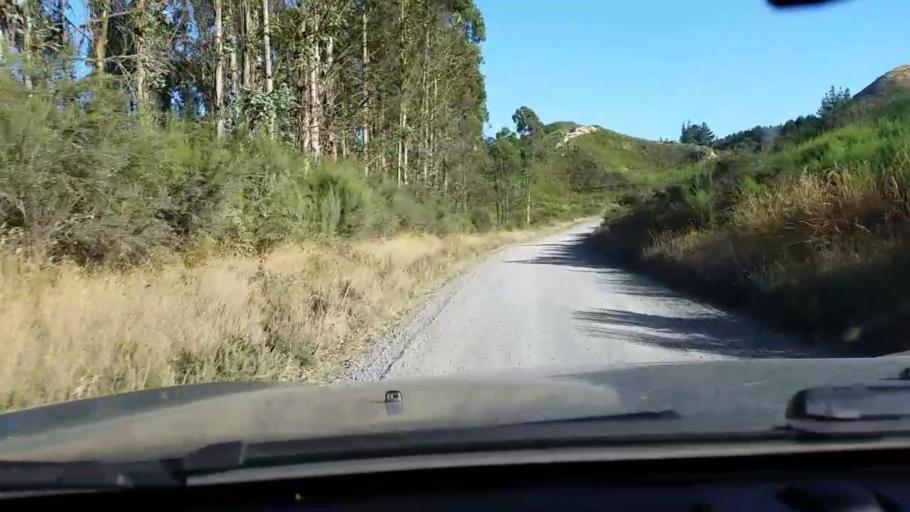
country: NZ
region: Waikato
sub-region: Taupo District
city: Taupo
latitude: -38.4624
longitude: 176.1599
